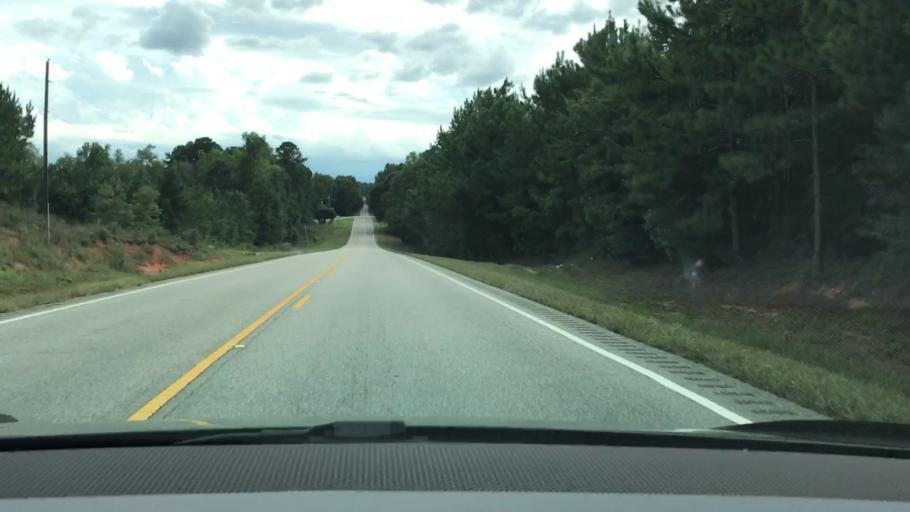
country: US
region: Alabama
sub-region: Pike County
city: Troy
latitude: 31.6285
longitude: -85.9757
